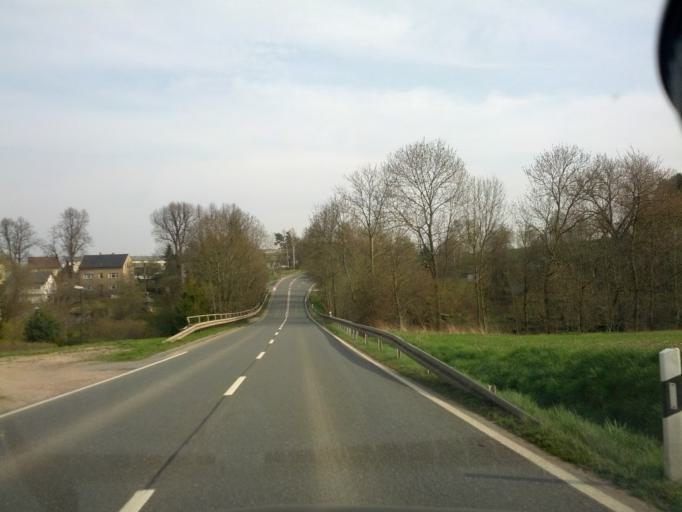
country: DE
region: Saxony
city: Kirchberg
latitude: 50.6469
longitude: 12.5631
